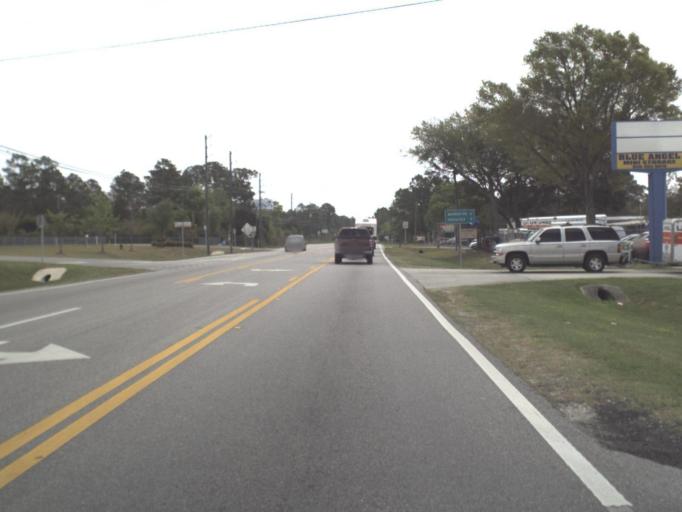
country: US
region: Florida
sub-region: Escambia County
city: Myrtle Grove
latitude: 30.3610
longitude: -87.3577
